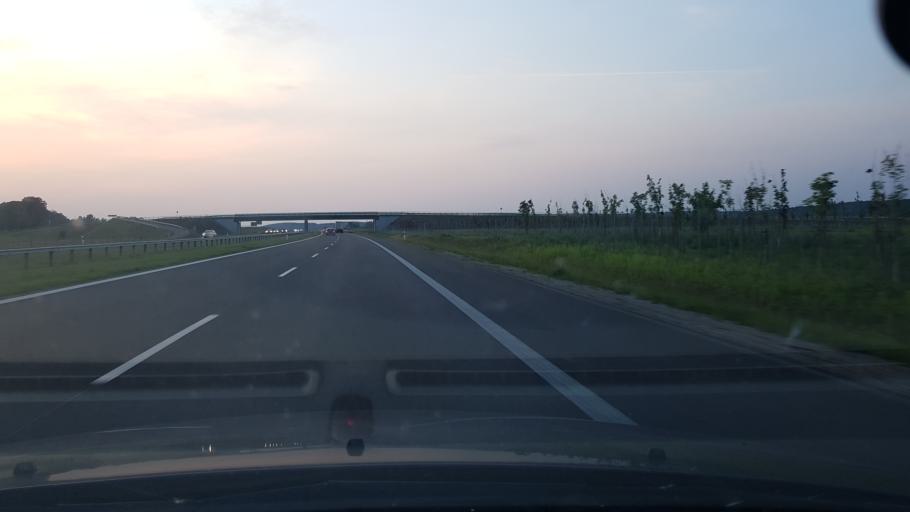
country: PL
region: Warmian-Masurian Voivodeship
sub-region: Powiat nidzicki
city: Nidzica
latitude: 53.3875
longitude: 20.3701
